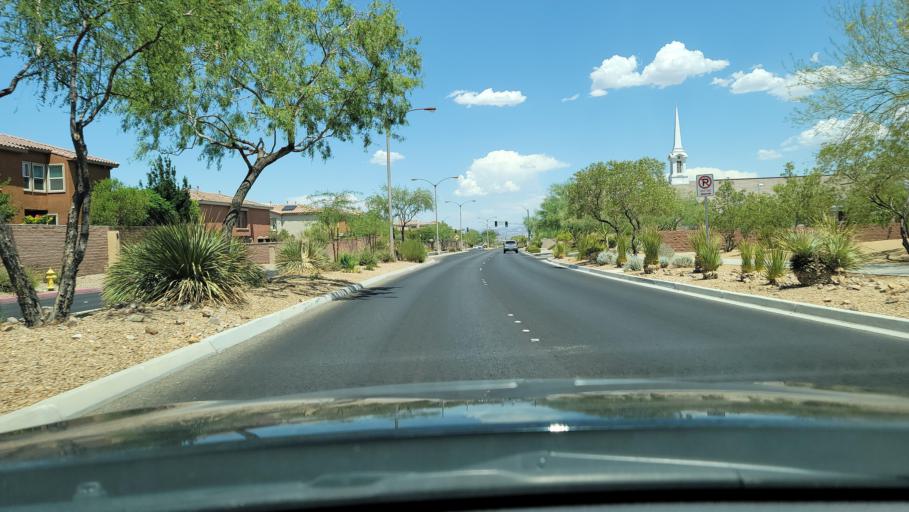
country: US
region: Nevada
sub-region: Clark County
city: Enterprise
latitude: 36.0052
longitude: -115.2670
